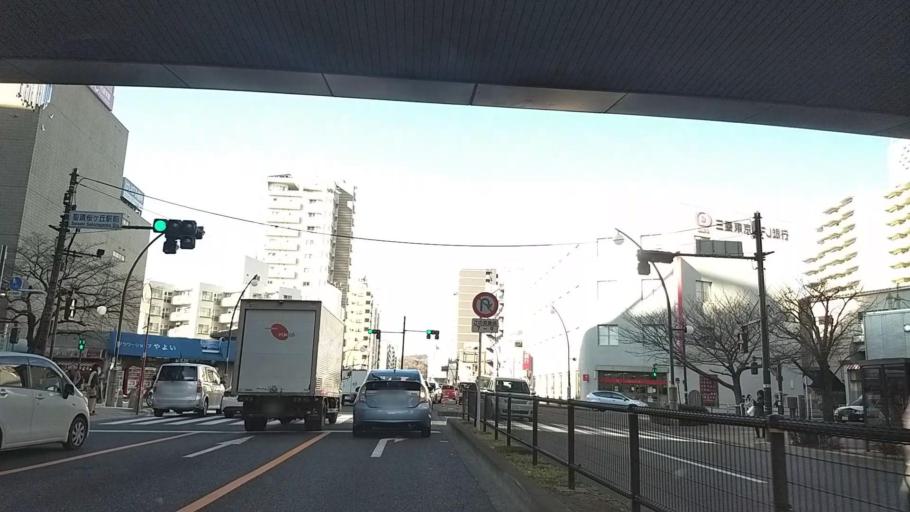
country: JP
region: Tokyo
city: Hino
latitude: 35.6502
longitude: 139.4469
